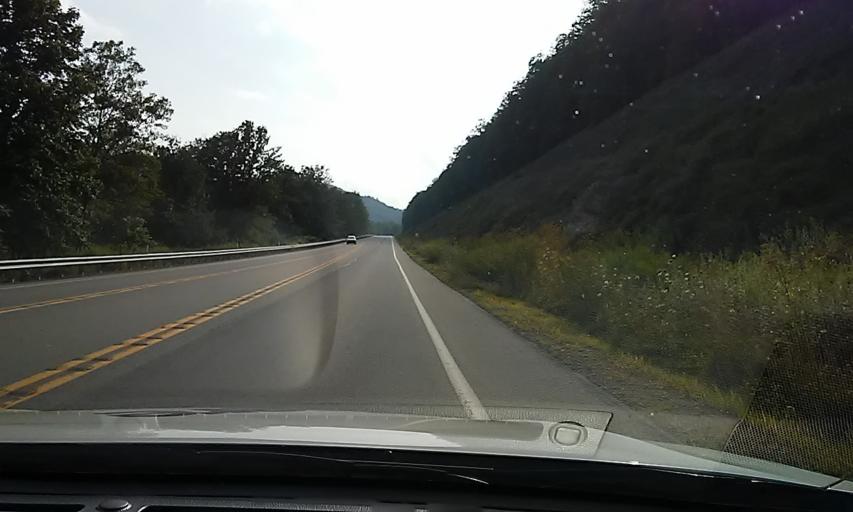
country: US
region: Pennsylvania
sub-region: Potter County
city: Coudersport
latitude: 41.7775
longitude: -77.8297
